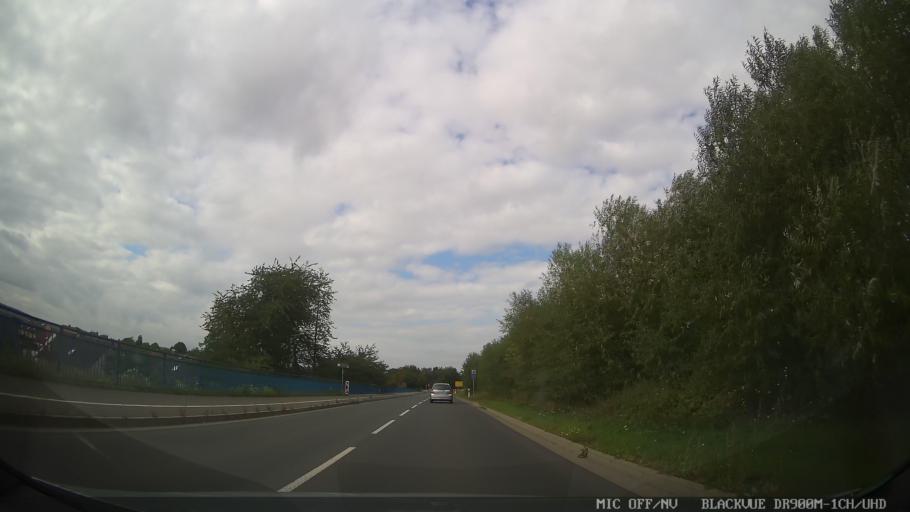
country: DE
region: Lower Saxony
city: Cramme
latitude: 52.1208
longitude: 10.4298
